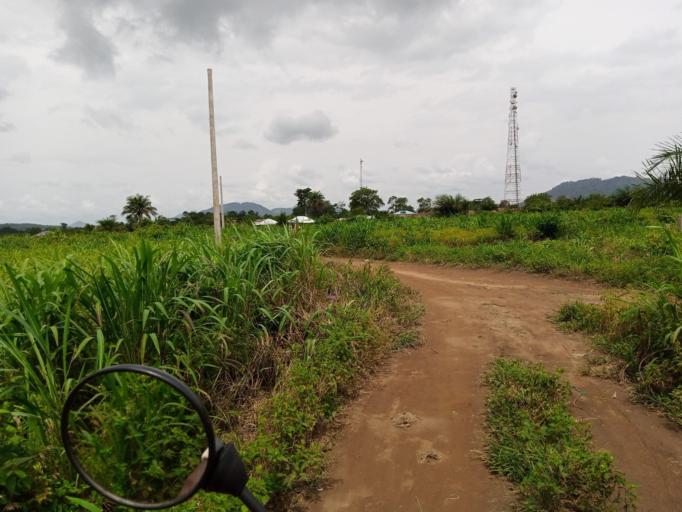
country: SL
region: Southern Province
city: Moyamba
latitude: 8.1684
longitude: -12.4172
